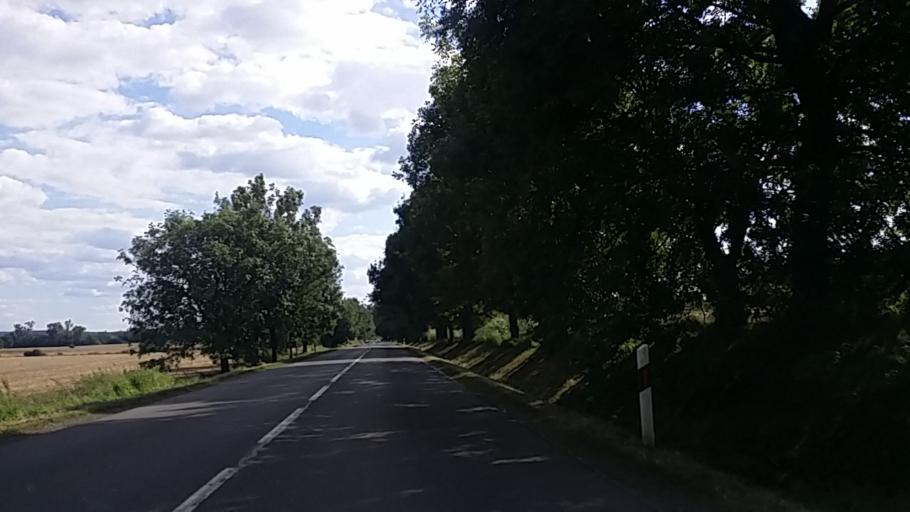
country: HU
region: Baranya
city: Sasd
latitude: 46.2764
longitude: 18.1065
